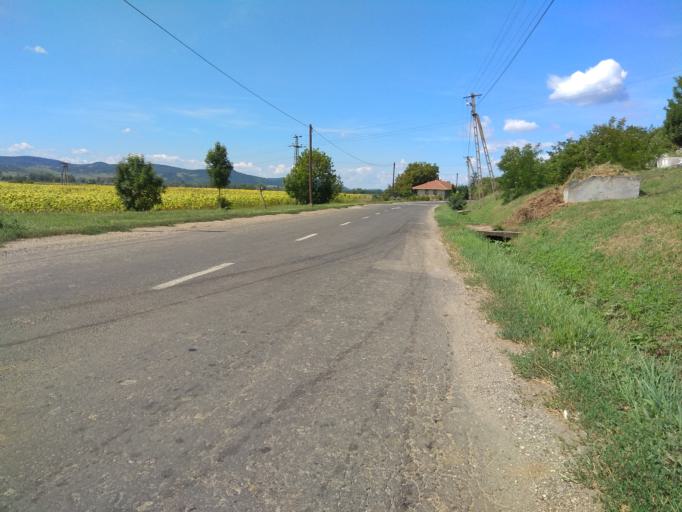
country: HU
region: Borsod-Abauj-Zemplen
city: Izsofalva
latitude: 48.2788
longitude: 20.6482
